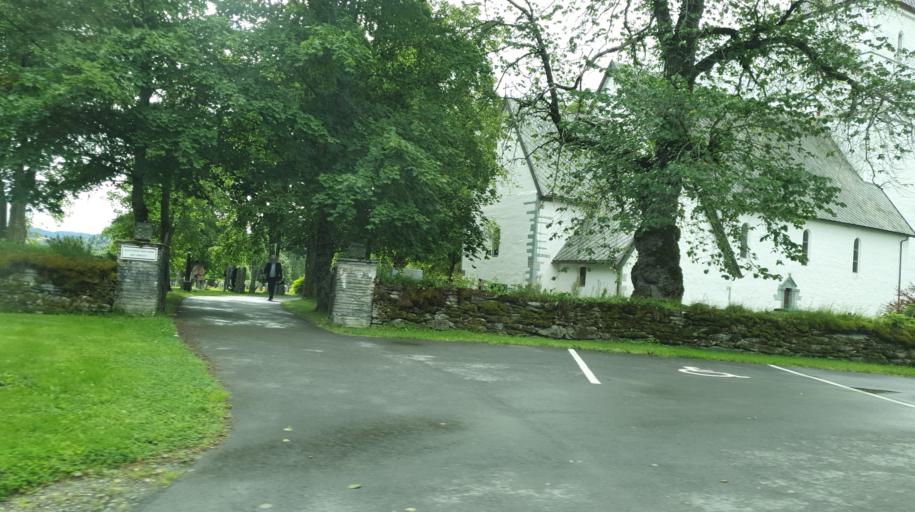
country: NO
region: Nord-Trondelag
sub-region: Stjordal
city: Stjordalshalsen
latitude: 63.4546
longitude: 10.9560
